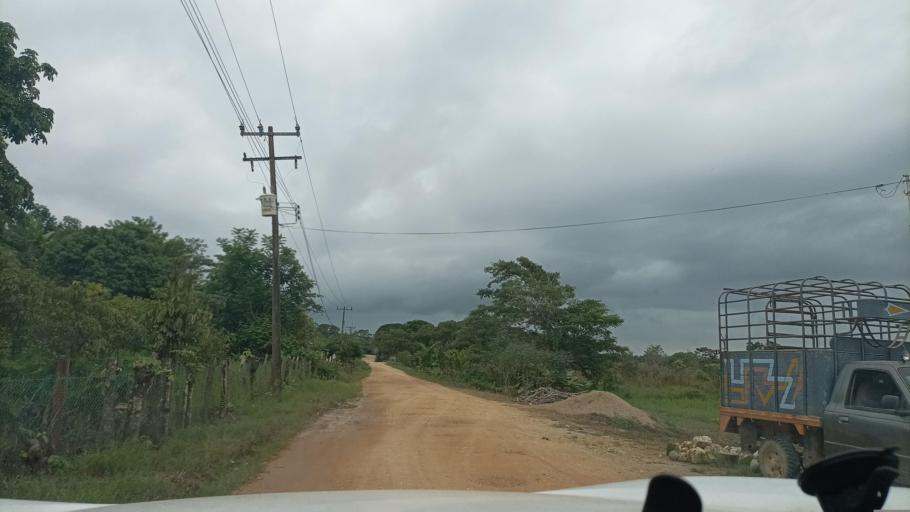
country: MX
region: Veracruz
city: Hidalgotitlan
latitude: 17.6415
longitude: -94.5119
